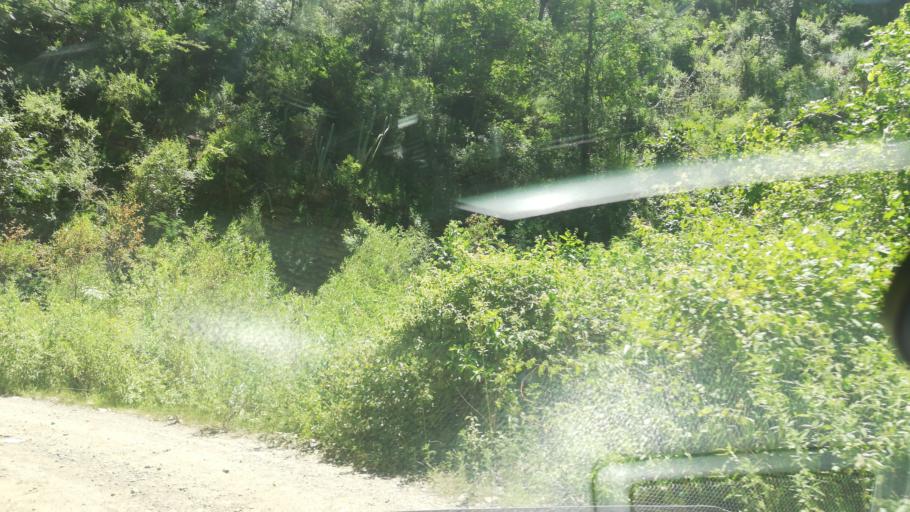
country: BO
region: Cochabamba
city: Mizque
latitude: -17.8286
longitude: -65.3003
